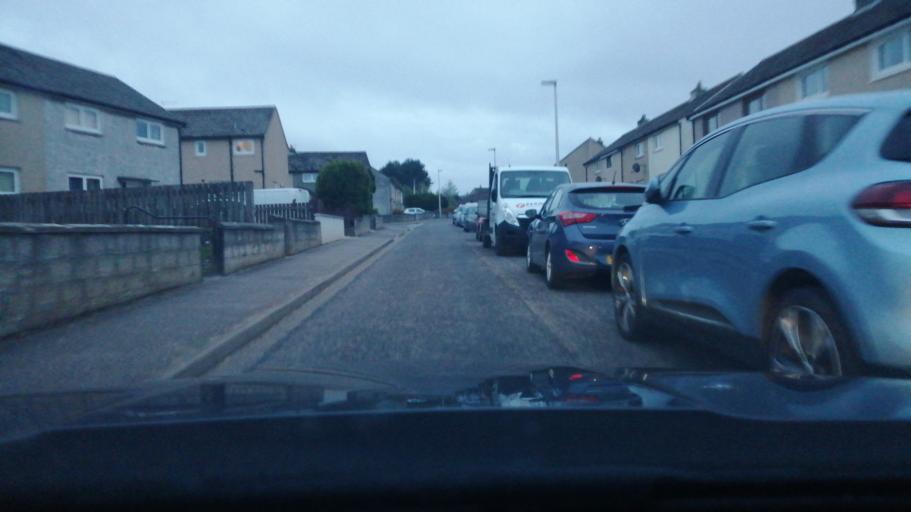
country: GB
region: Scotland
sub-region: Moray
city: Keith
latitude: 57.5392
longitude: -2.9565
